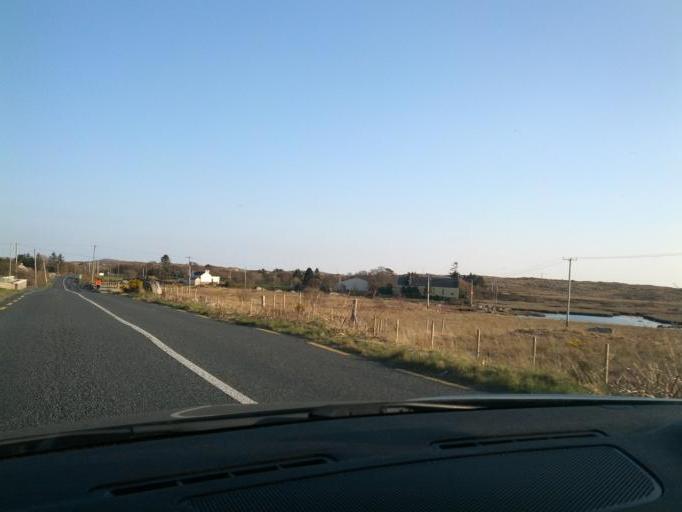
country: IE
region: Connaught
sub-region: County Galway
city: Oughterard
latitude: 53.3783
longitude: -9.5481
